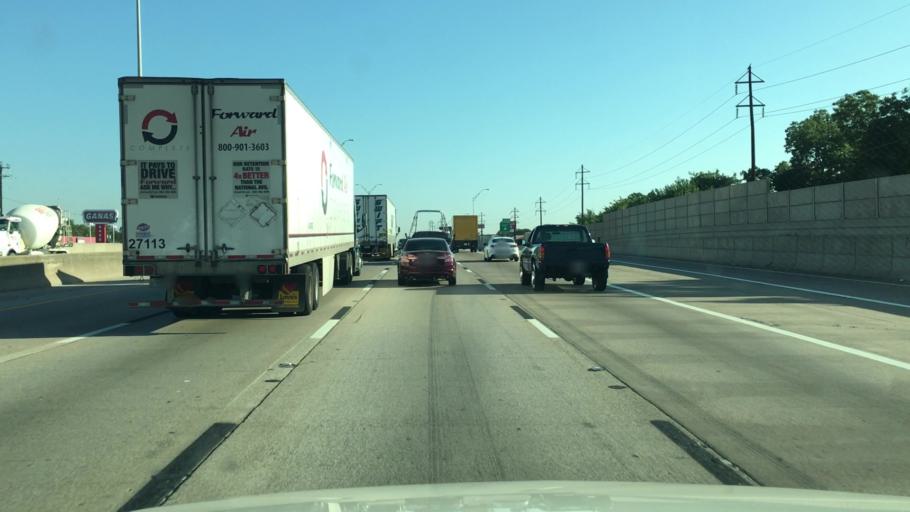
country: US
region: Texas
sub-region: Tarrant County
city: Edgecliff Village
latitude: 32.6790
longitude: -97.3202
